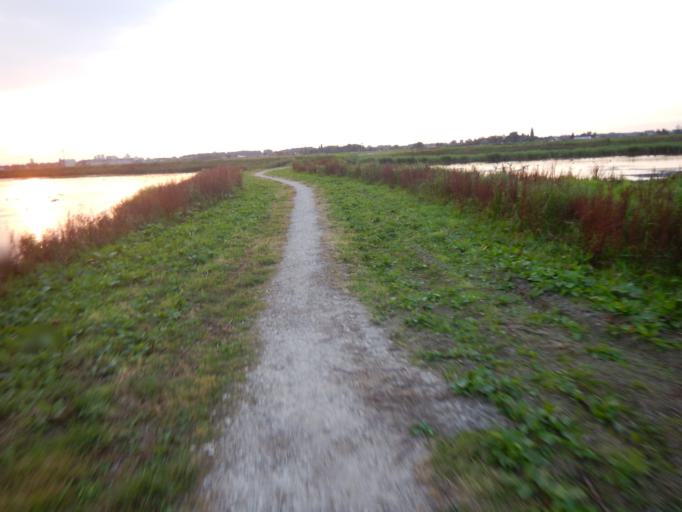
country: NL
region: South Holland
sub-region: Gemeente Pijnacker-Nootdorp
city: Pijnacker
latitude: 52.0680
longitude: 4.4354
